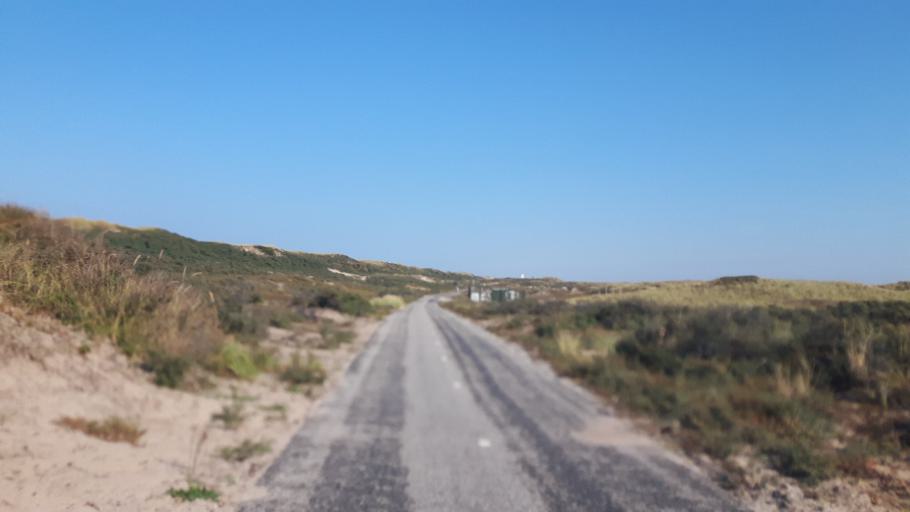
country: NL
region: North Holland
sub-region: Gemeente Zandvoort
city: Zandvoort
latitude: 52.3359
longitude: 4.5032
